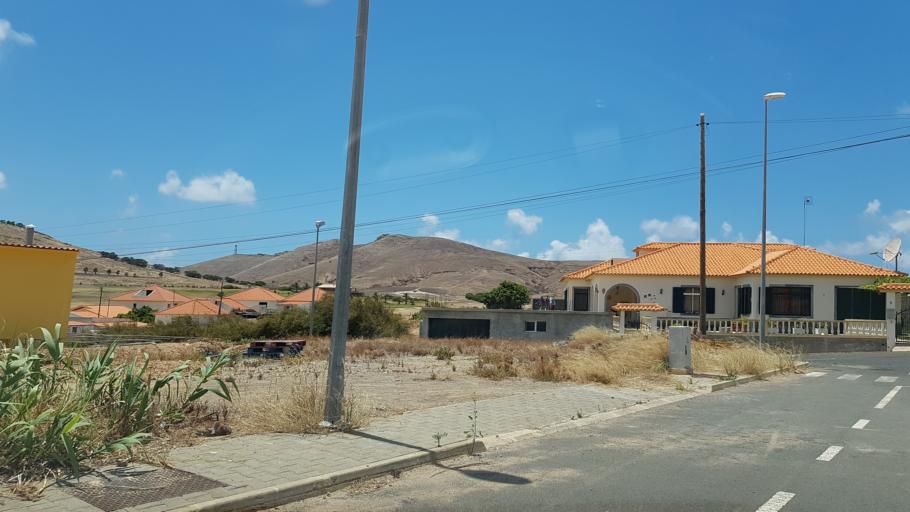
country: PT
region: Madeira
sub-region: Porto Santo
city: Vila de Porto Santo
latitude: 33.0554
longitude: -16.3654
